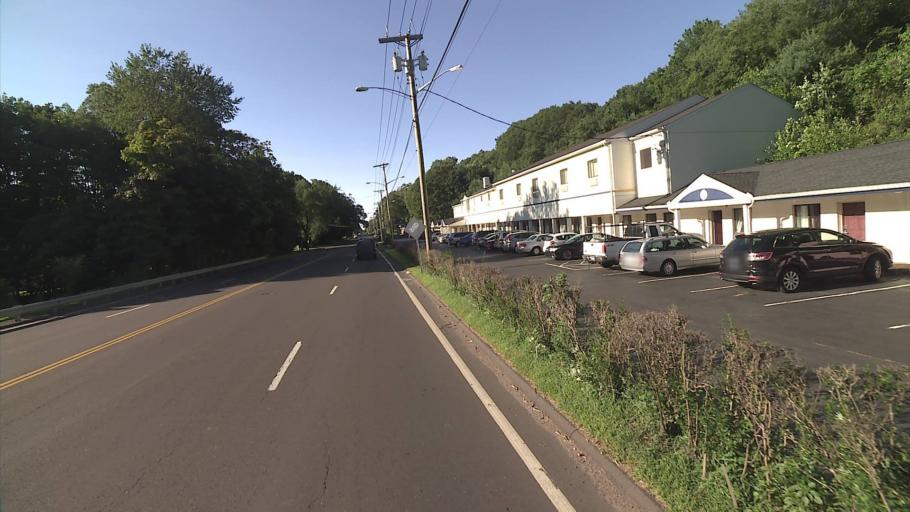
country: US
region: Connecticut
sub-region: New Haven County
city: Hamden
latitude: 41.4195
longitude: -72.9042
